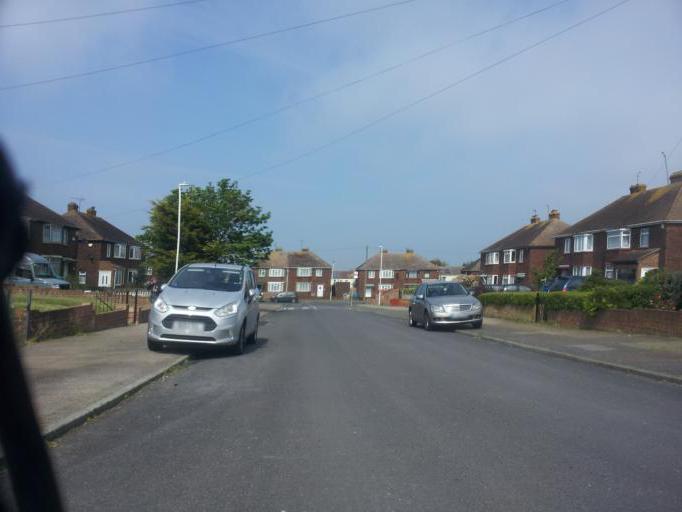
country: GB
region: England
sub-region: Kent
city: Queenborough
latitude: 51.4085
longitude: 0.7412
